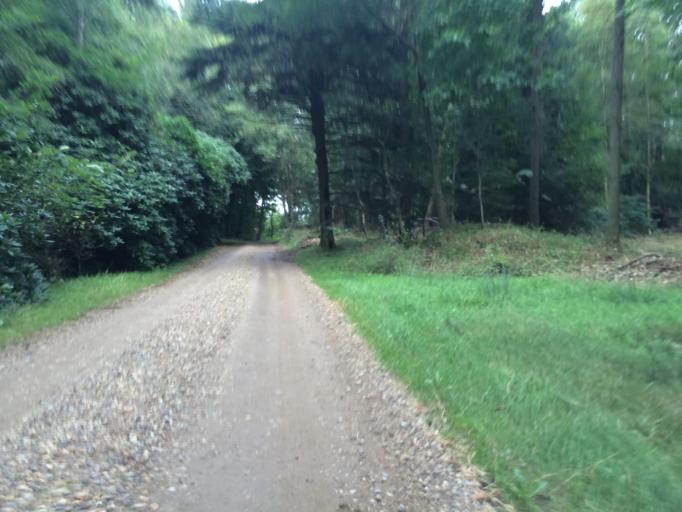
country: DK
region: Central Jutland
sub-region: Holstebro Kommune
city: Ulfborg
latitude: 56.2230
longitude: 8.4065
